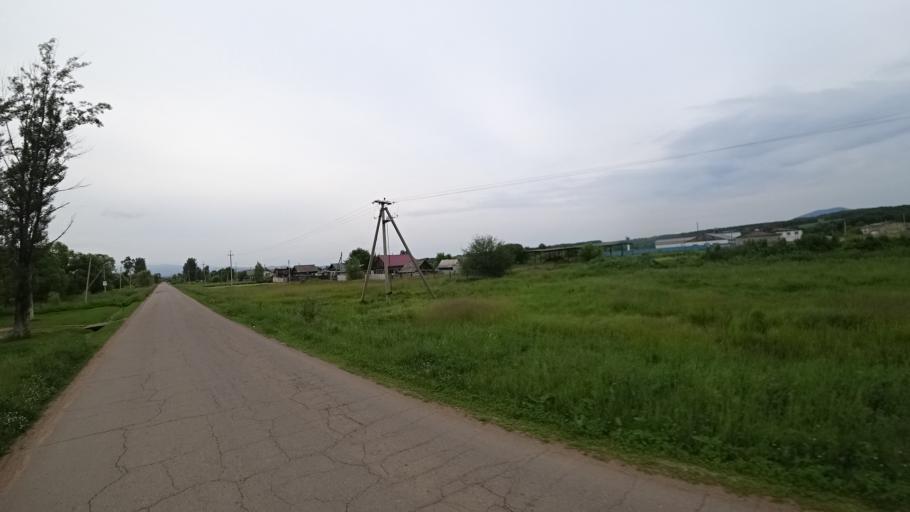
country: RU
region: Primorskiy
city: Novosysoyevka
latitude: 44.2350
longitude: 133.3702
